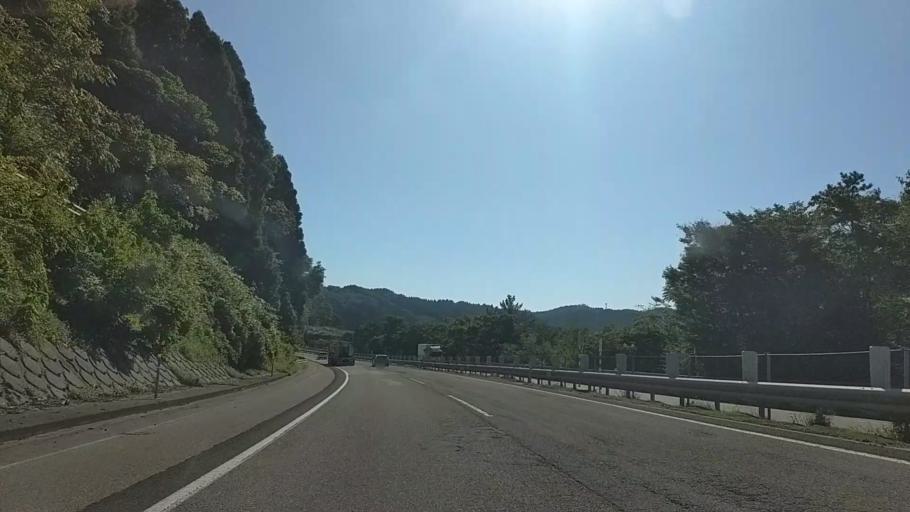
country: JP
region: Ishikawa
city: Tsubata
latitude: 36.5981
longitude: 136.7361
